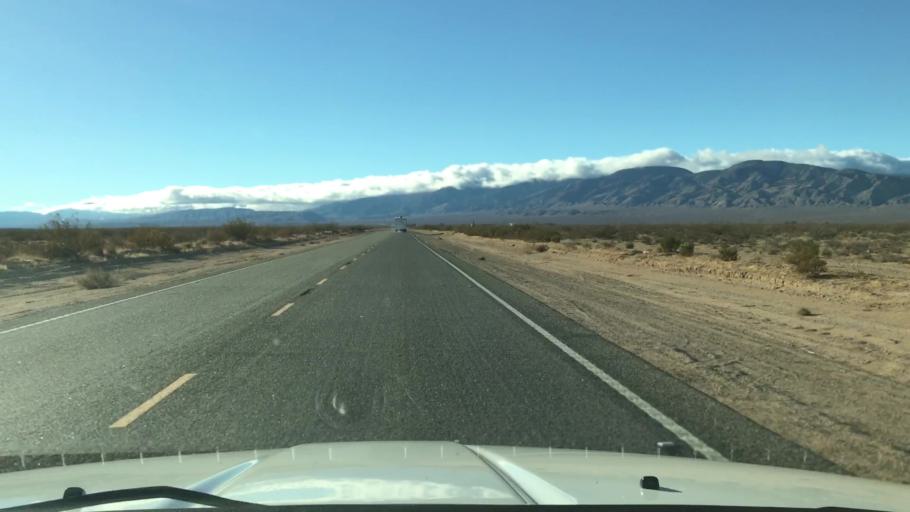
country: US
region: California
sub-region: Kern County
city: California City
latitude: 35.1255
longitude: -118.0678
